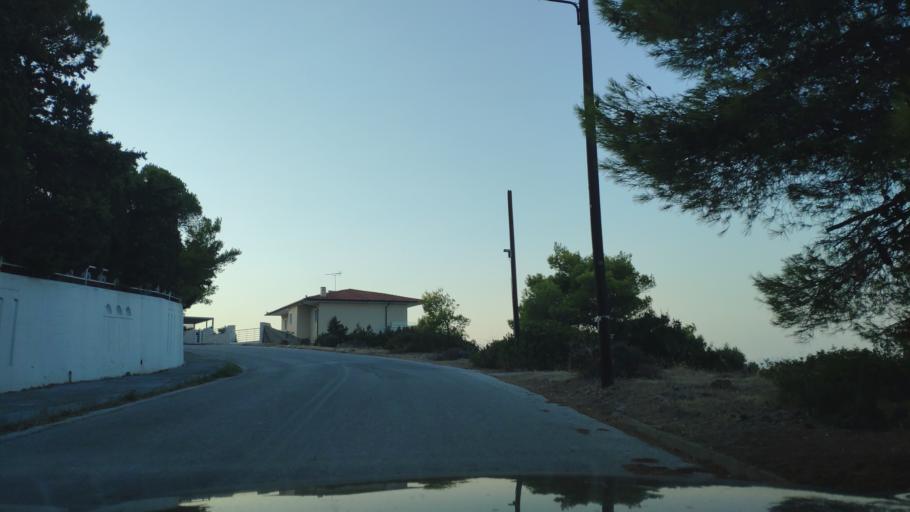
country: GR
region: Attica
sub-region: Nomarchia Anatolikis Attikis
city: Limin Mesoyaias
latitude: 37.9152
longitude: 24.0230
